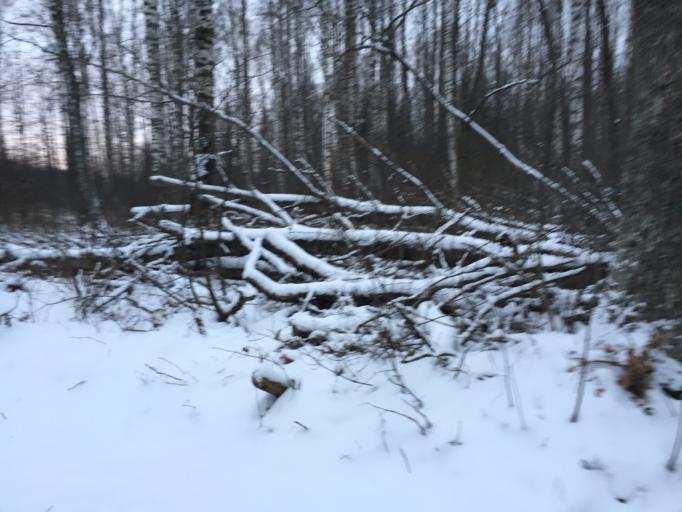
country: LV
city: Tireli
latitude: 56.9286
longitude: 23.5670
